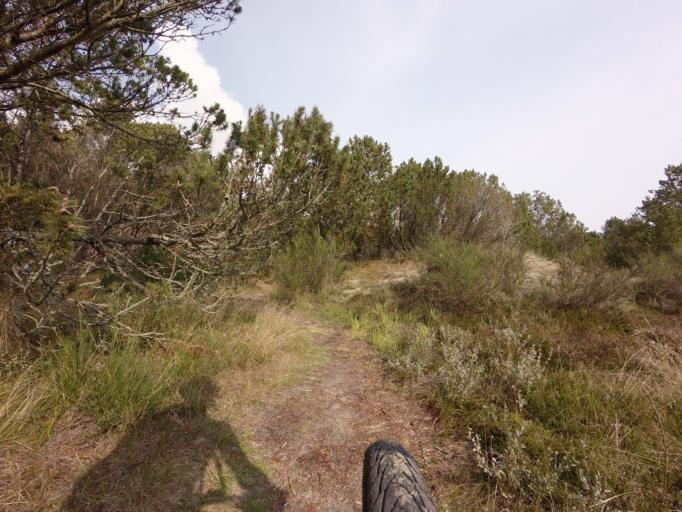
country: DK
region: North Denmark
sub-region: Frederikshavn Kommune
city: Strandby
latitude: 57.6425
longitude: 10.4119
